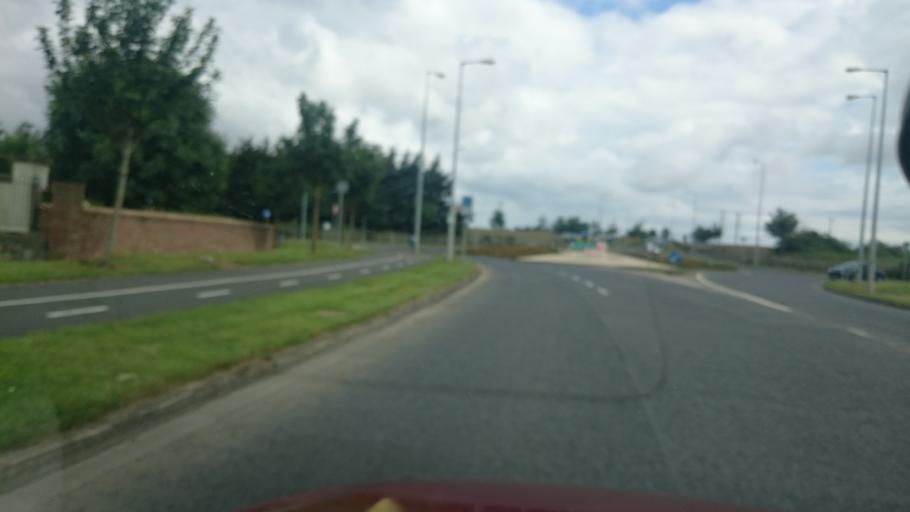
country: IE
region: Leinster
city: Lusk
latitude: 53.5231
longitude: -6.1580
